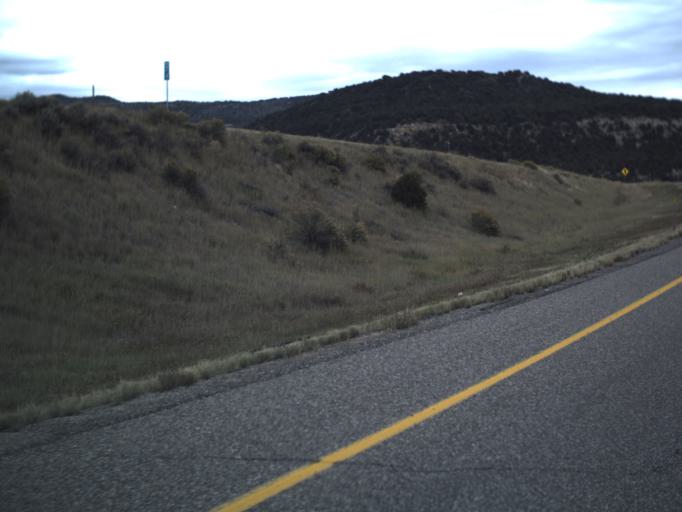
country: US
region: Utah
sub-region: Sevier County
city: Salina
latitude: 38.8780
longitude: -111.5643
